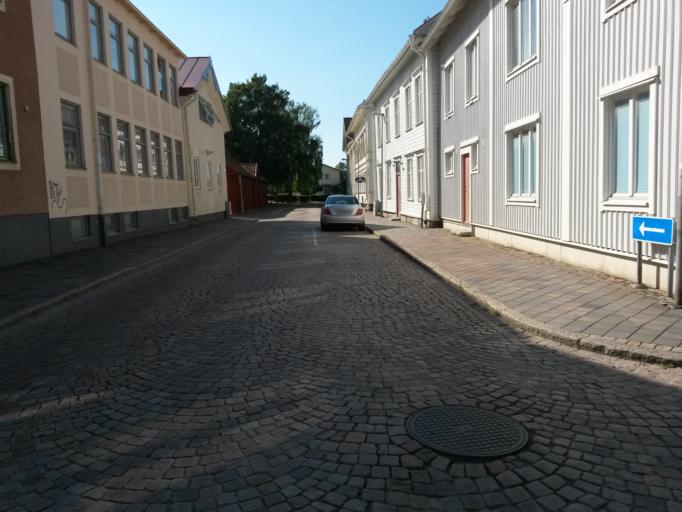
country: SE
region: Vaestra Goetaland
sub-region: Lidkopings Kommun
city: Lidkoping
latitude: 58.5052
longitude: 13.1550
